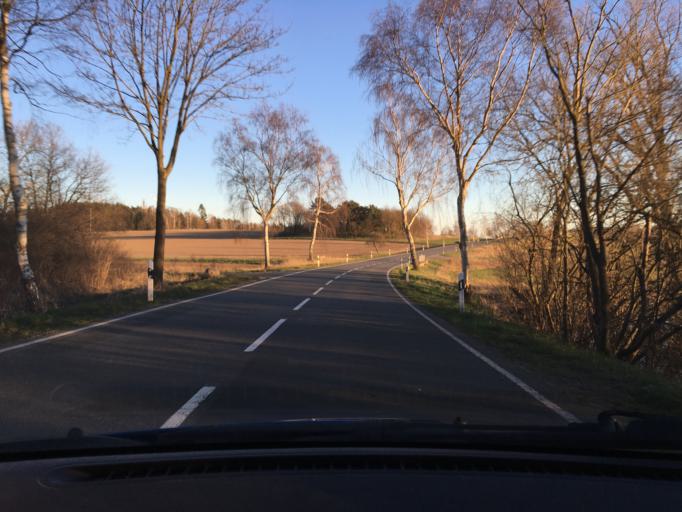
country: DE
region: Lower Saxony
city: Dahlem
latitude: 53.1957
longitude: 10.7523
